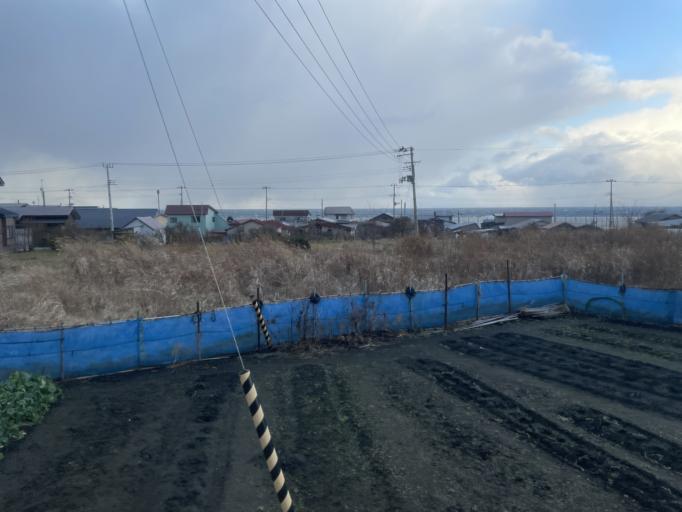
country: JP
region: Aomori
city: Mutsu
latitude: 41.0909
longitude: 141.2496
